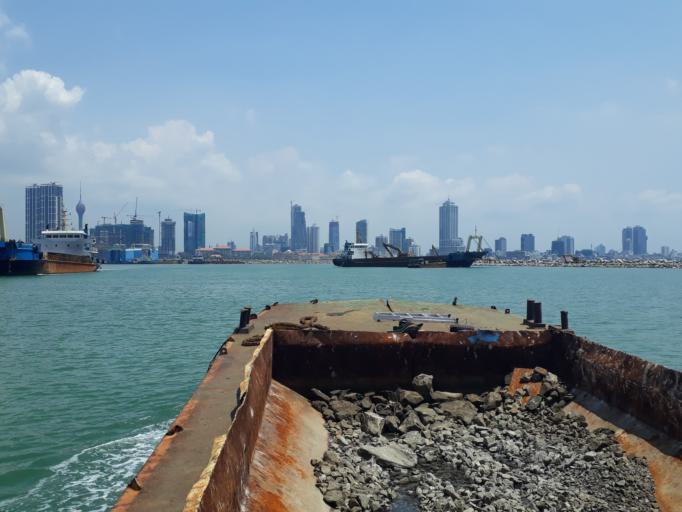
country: LK
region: Western
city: Colombo
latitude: 6.9241
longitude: 79.8272
